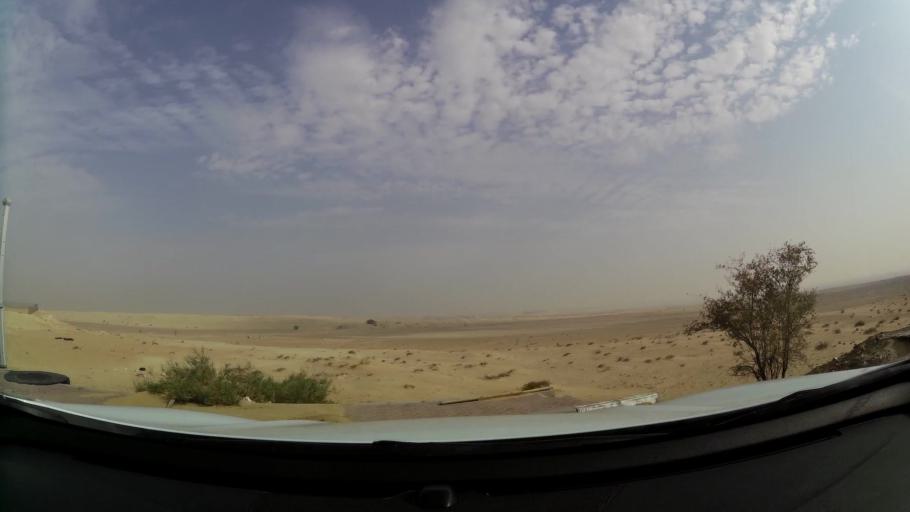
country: AE
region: Abu Dhabi
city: Abu Dhabi
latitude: 24.2569
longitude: 54.7221
